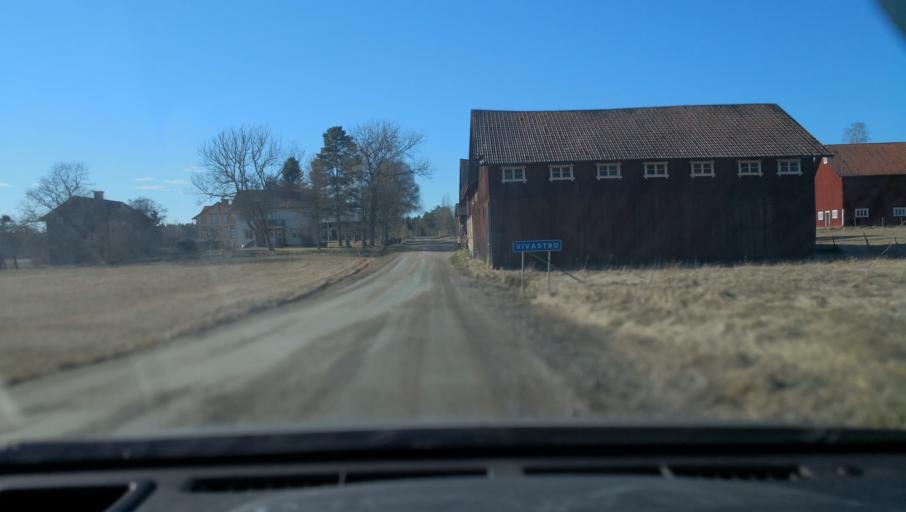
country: SE
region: Vaestmanland
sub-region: Sala Kommun
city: Sala
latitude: 60.1520
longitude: 16.6364
